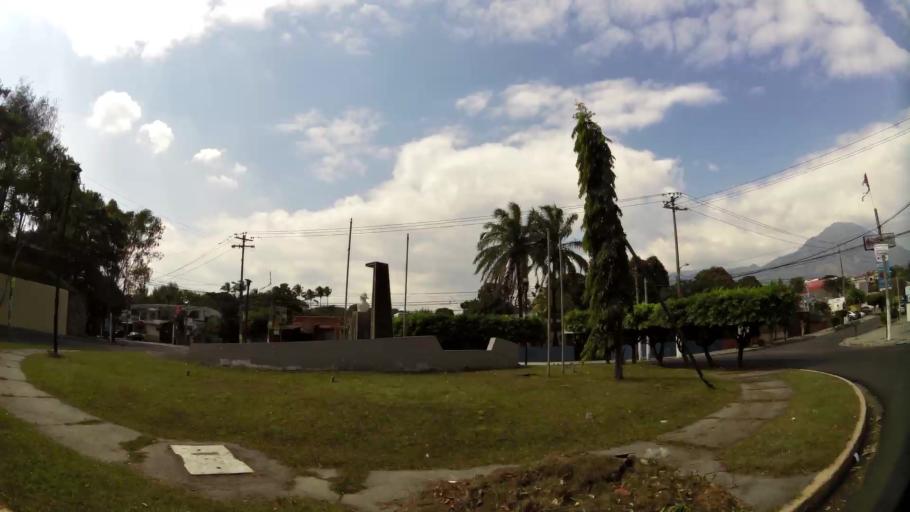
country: SV
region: San Salvador
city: Mejicanos
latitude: 13.7063
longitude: -89.2190
